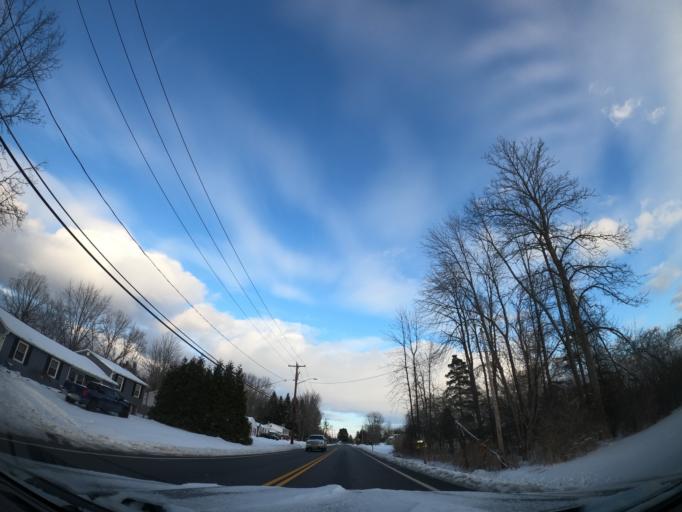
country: US
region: New York
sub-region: Onondaga County
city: Brewerton
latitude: 43.2306
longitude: -76.1177
